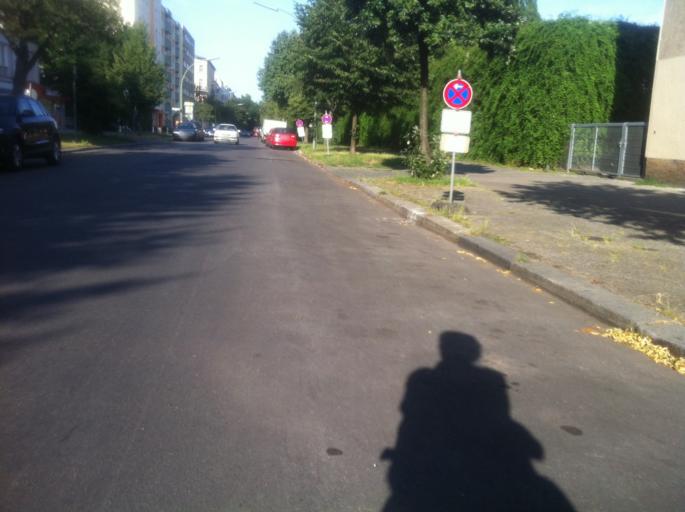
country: DE
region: Berlin
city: Berlin Schoeneberg
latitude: 52.4968
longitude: 13.3480
